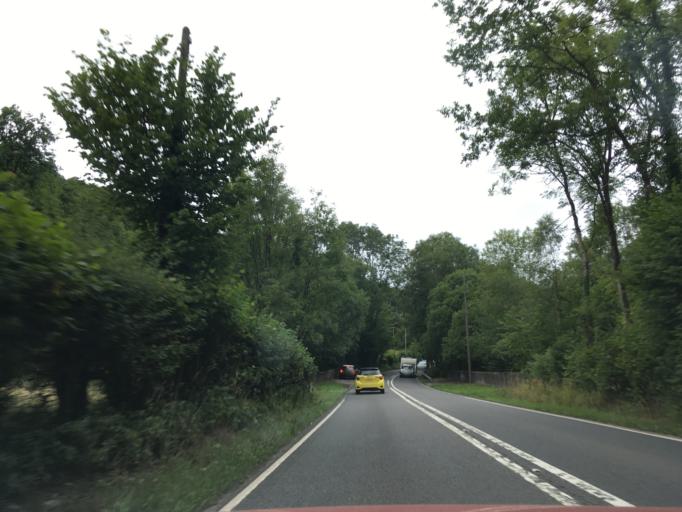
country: GB
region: Wales
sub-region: Carmarthenshire
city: Llandovery
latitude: 51.9899
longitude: -3.7308
